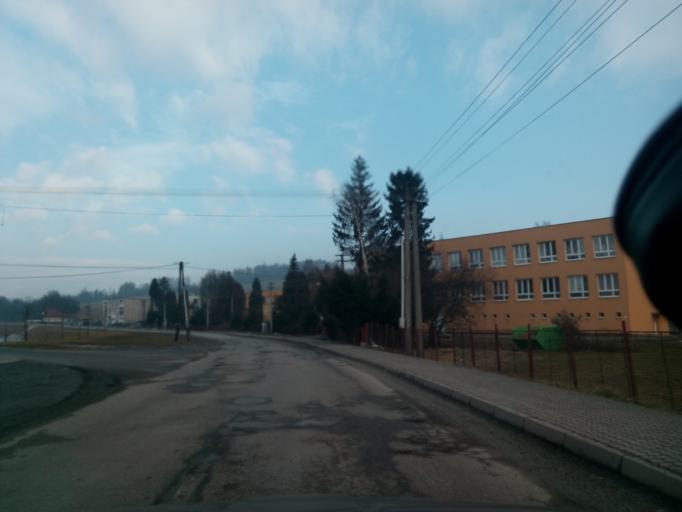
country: SK
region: Presovsky
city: Lipany
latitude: 49.1739
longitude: 20.8703
